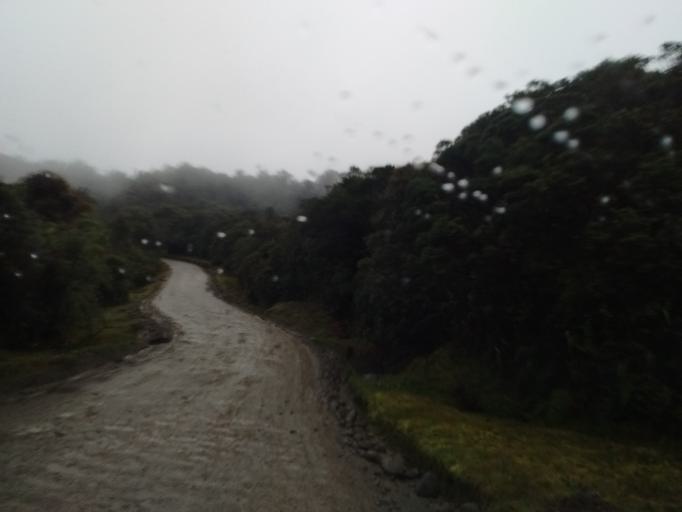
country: CO
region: Cauca
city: Paispamba
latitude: 2.1639
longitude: -76.4206
